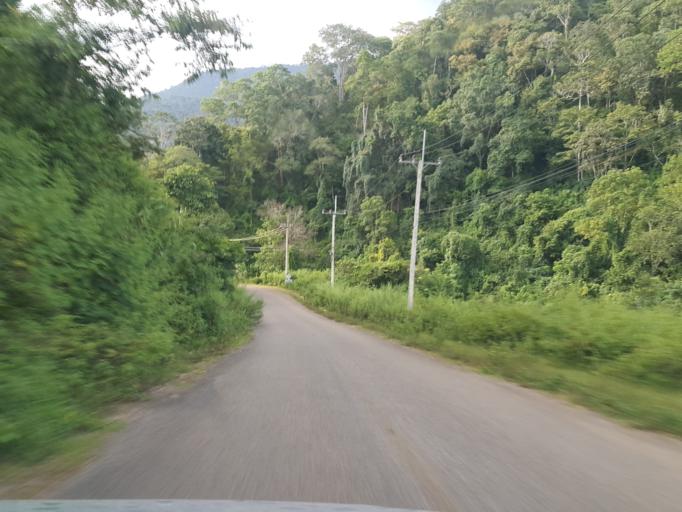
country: TH
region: Mae Hong Son
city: Khun Yuam
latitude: 18.7490
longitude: 98.1961
